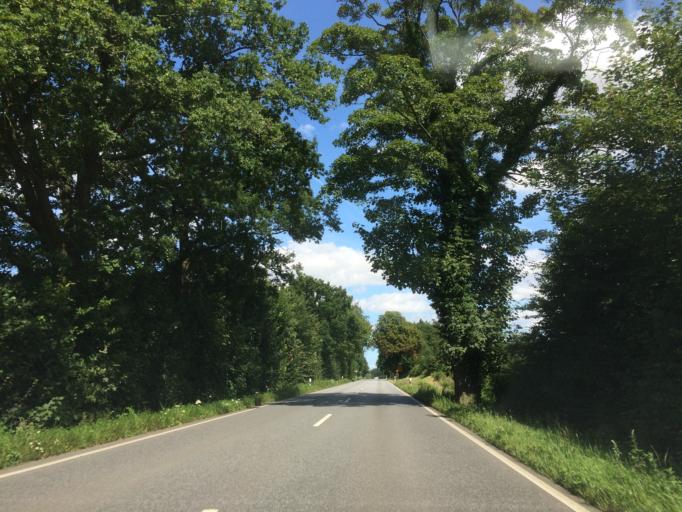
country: DE
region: Schleswig-Holstein
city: Grebin
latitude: 54.1982
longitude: 10.4695
